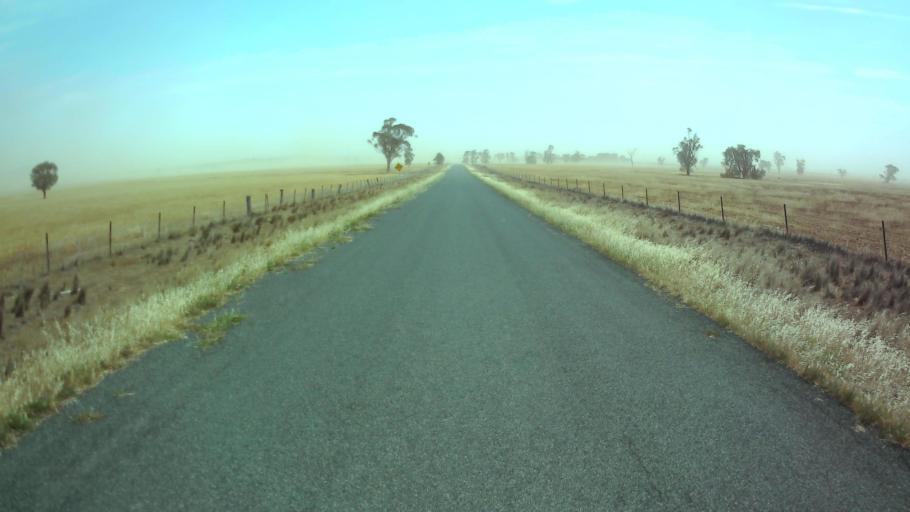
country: AU
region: New South Wales
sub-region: Weddin
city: Grenfell
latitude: -33.7431
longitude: 147.9922
